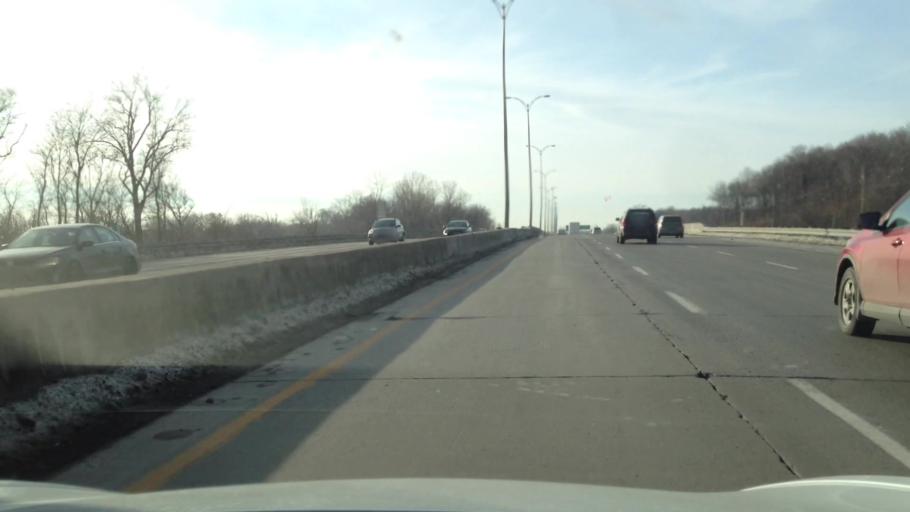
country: CA
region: Quebec
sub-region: Monteregie
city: Vaudreuil-Dorion
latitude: 45.4187
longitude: -74.0024
